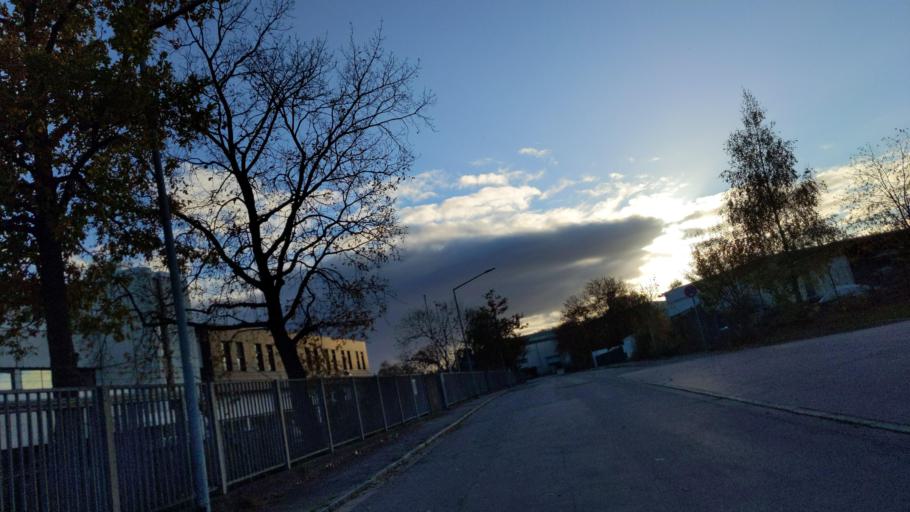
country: DE
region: Schleswig-Holstein
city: Neustadt in Holstein
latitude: 54.0963
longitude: 10.7925
